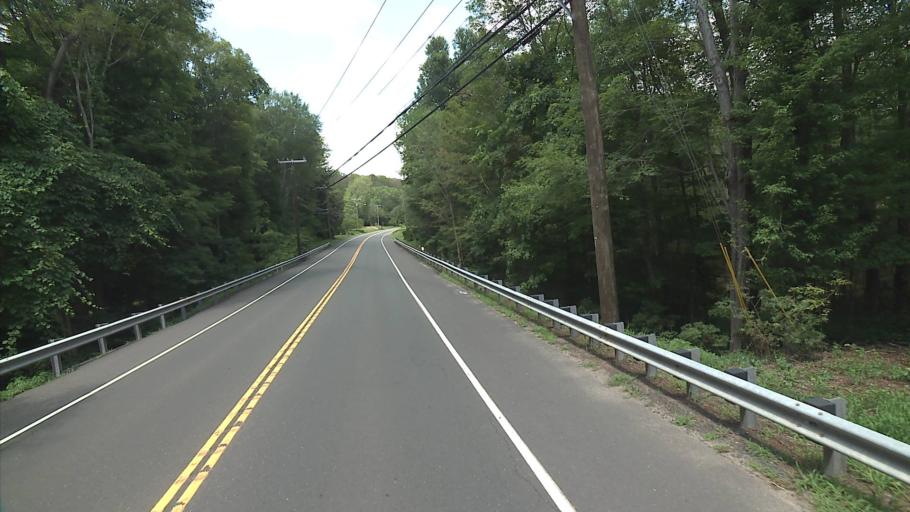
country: US
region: Connecticut
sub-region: Middlesex County
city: East Haddam
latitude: 41.4513
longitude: -72.4783
